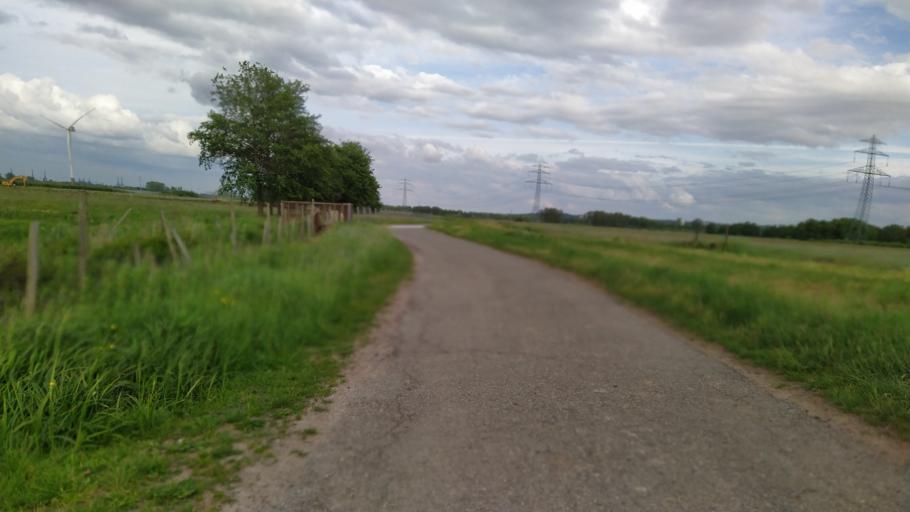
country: DE
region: Lower Saxony
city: Neu Wulmstorf
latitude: 53.4955
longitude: 9.8362
